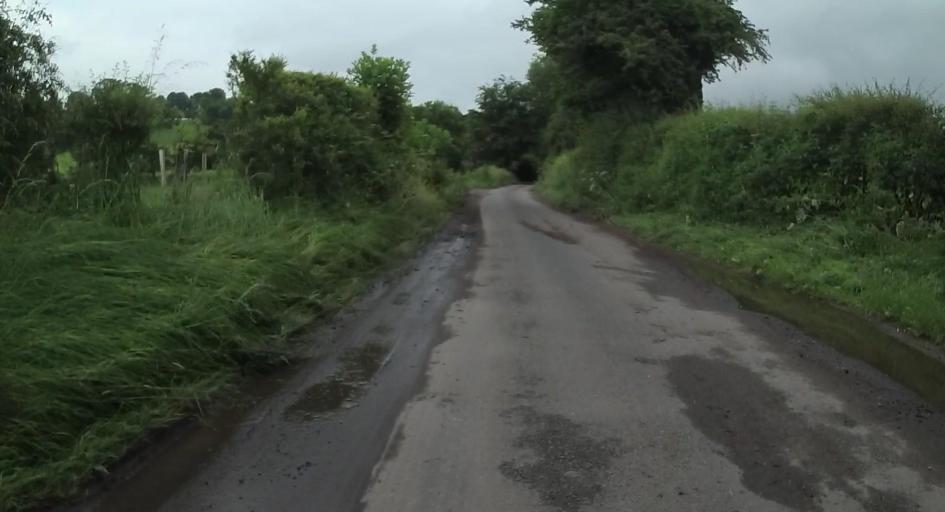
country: GB
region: England
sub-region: Hampshire
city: Kingsclere
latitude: 51.3298
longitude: -1.2883
